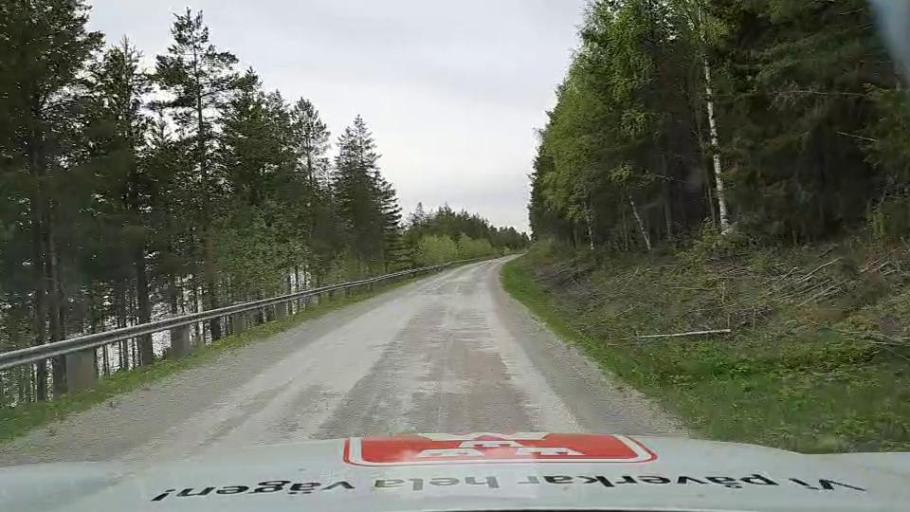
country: SE
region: Jaemtland
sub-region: Bergs Kommun
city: Hoverberg
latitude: 62.7245
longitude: 14.6684
